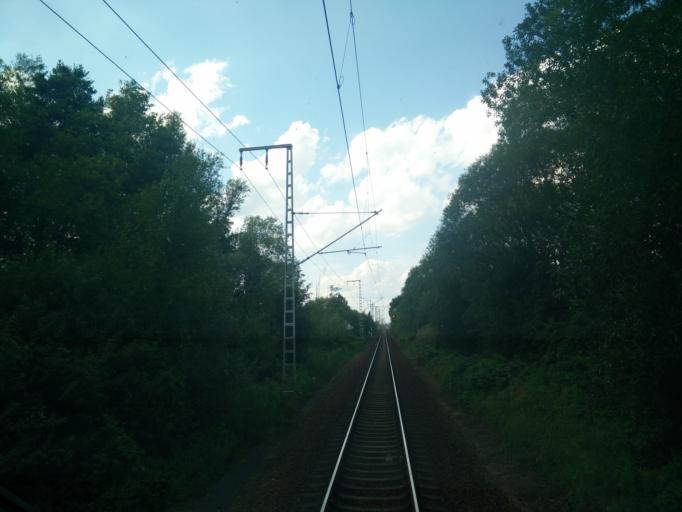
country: DE
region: Brandenburg
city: Lubbenau
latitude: 51.8572
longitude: 13.9727
